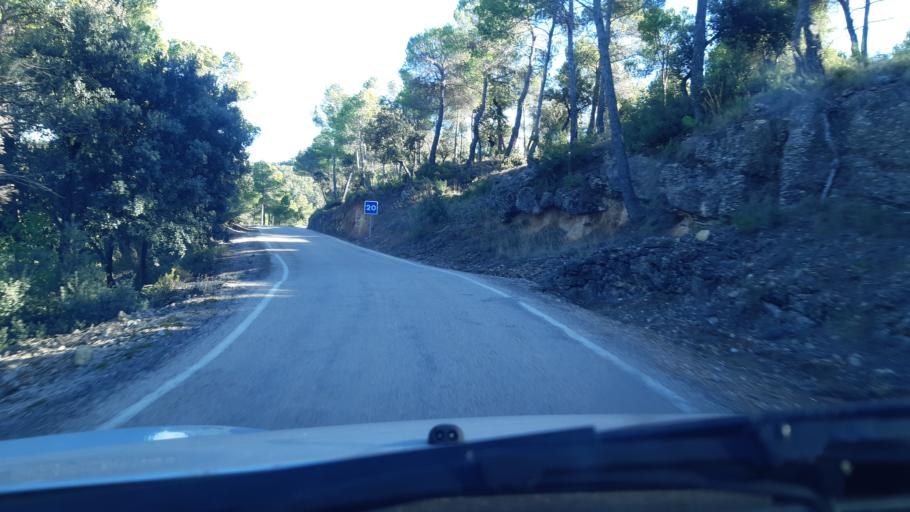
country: ES
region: Aragon
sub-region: Provincia de Teruel
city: Fornoles
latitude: 40.9038
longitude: -0.0058
